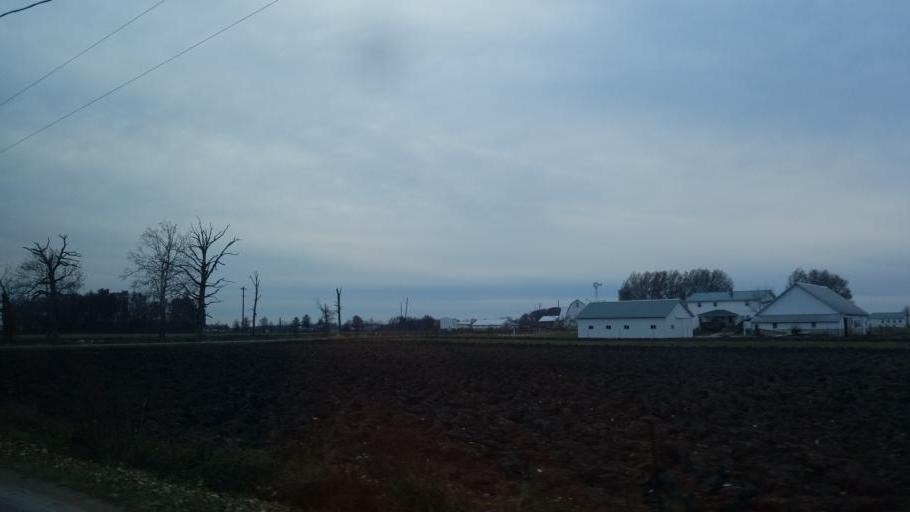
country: US
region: Indiana
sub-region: Adams County
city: Berne
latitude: 40.7032
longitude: -84.8793
